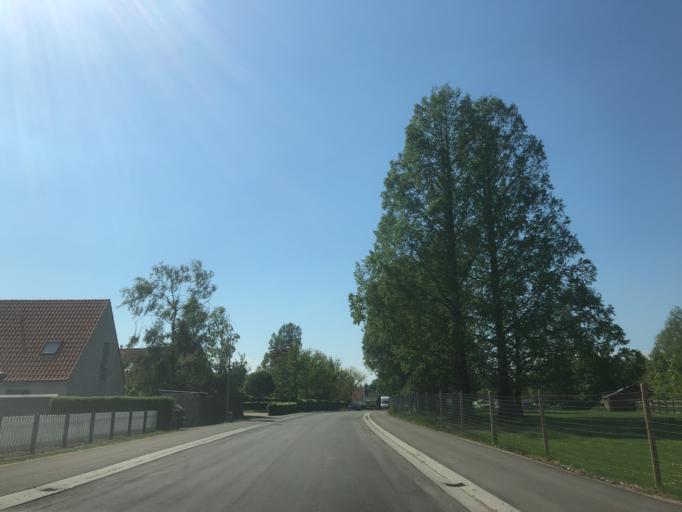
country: DK
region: Capital Region
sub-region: Hoje-Taastrup Kommune
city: Taastrup
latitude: 55.6263
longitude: 12.2536
